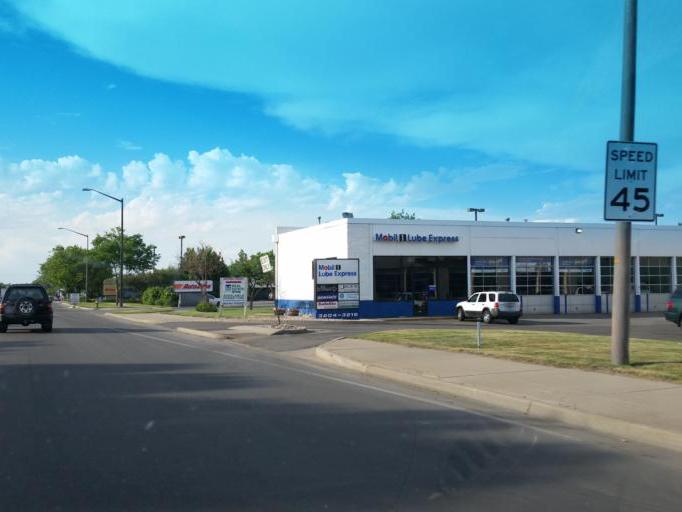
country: US
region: Colorado
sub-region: Larimer County
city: Loveland
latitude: 40.4254
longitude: -105.0775
